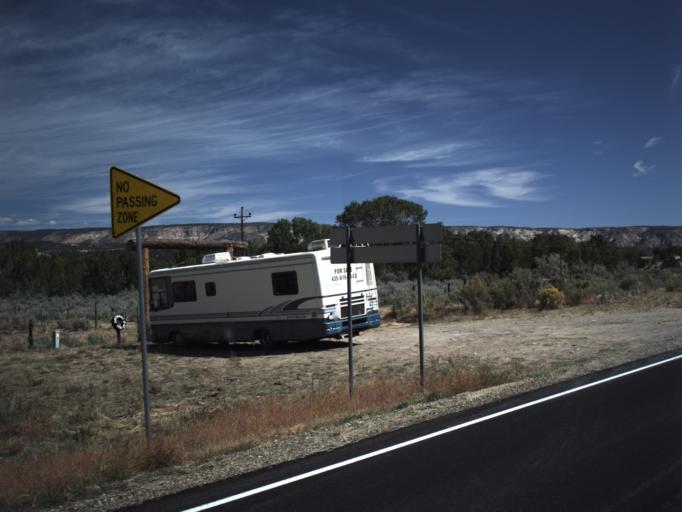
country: US
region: Utah
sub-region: Wayne County
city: Loa
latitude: 37.7651
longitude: -111.6799
